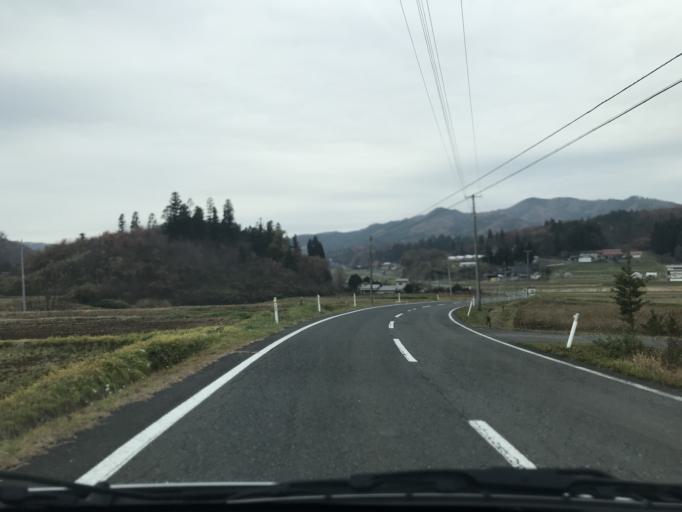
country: JP
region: Iwate
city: Kitakami
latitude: 39.2553
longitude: 141.2059
